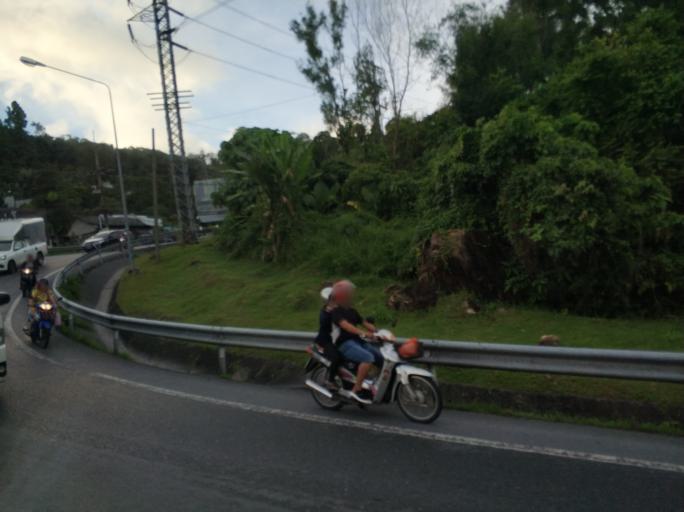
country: TH
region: Phuket
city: Kathu
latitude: 7.9044
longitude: 98.3245
